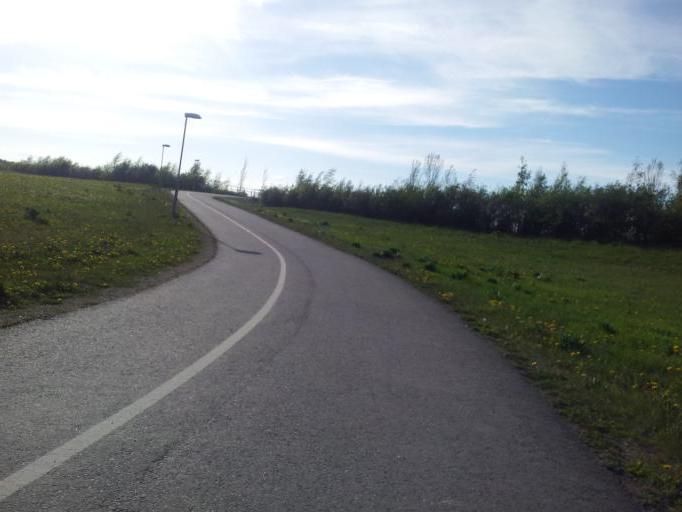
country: SE
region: Uppsala
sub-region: Uppsala Kommun
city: Gamla Uppsala
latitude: 59.8829
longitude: 17.6512
